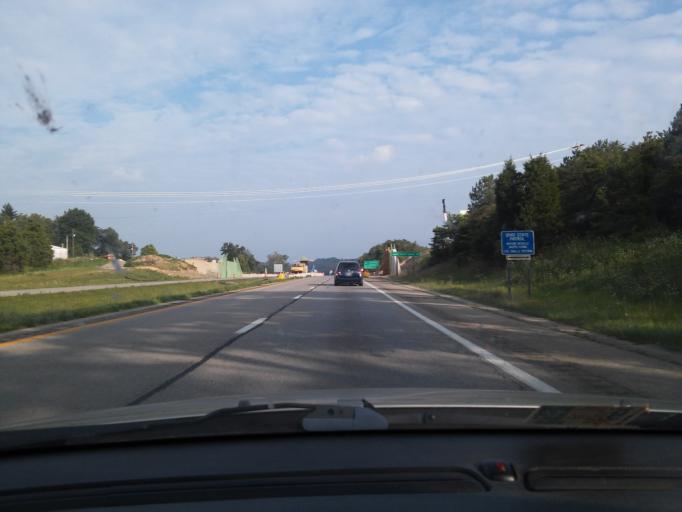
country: US
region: Ohio
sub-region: Jackson County
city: Jackson
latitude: 39.0375
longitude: -82.6030
